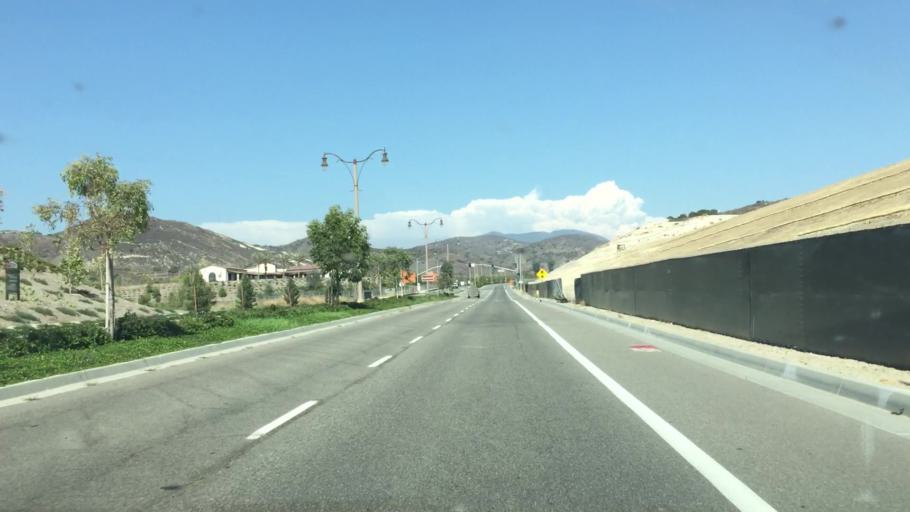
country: US
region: California
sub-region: Orange County
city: Foothill Ranch
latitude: 33.6943
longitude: -117.7037
